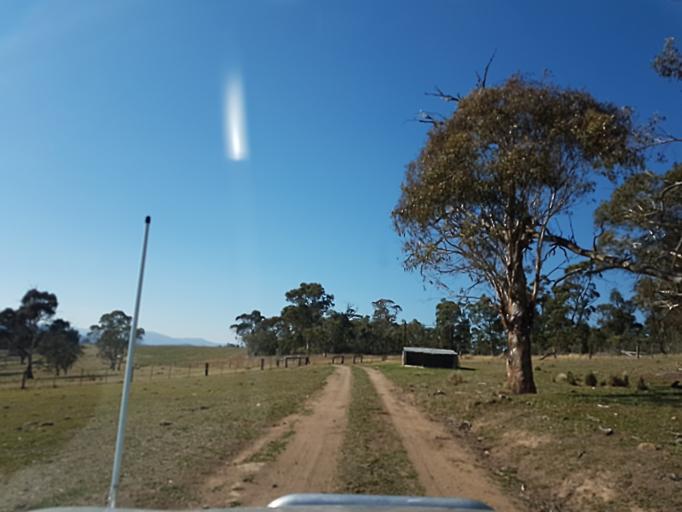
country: AU
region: New South Wales
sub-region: Snowy River
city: Jindabyne
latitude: -37.0419
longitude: 148.2840
